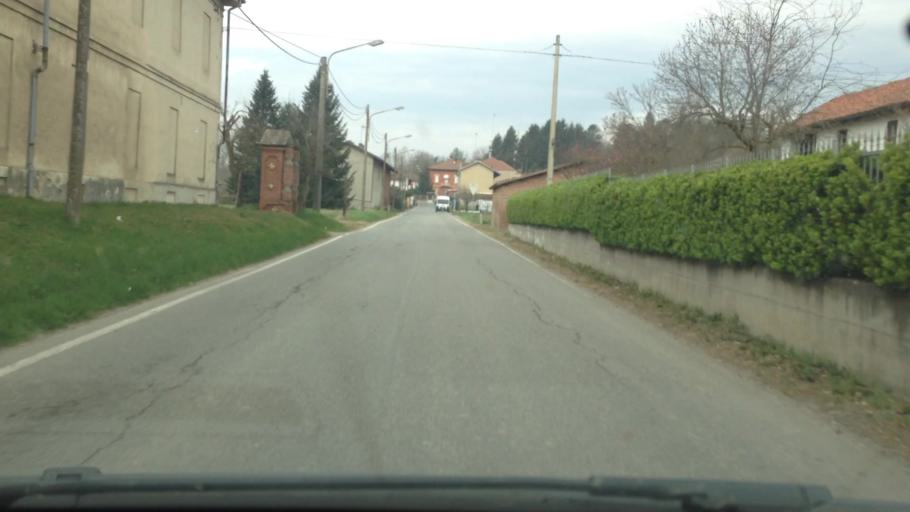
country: IT
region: Piedmont
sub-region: Provincia di Asti
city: Revigliasco d'Asti
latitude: 44.8902
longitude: 8.1435
